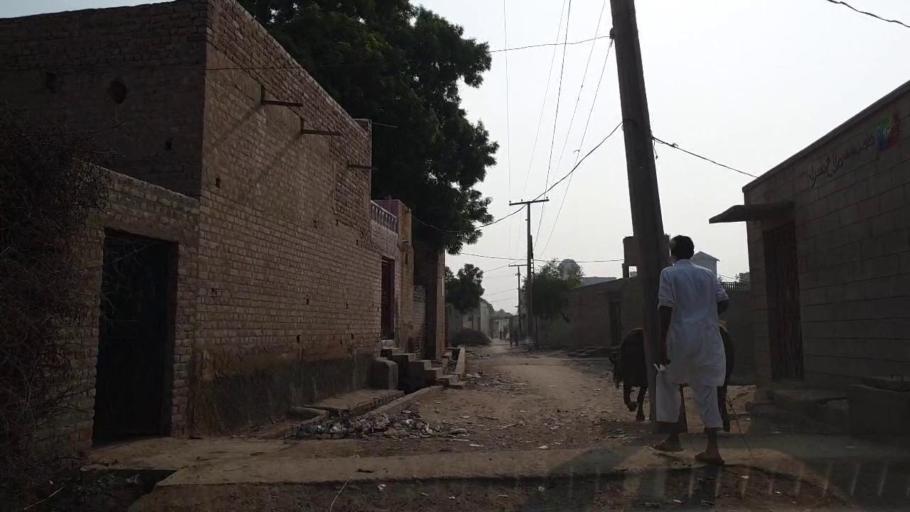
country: PK
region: Sindh
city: Bhan
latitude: 26.5798
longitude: 67.7299
